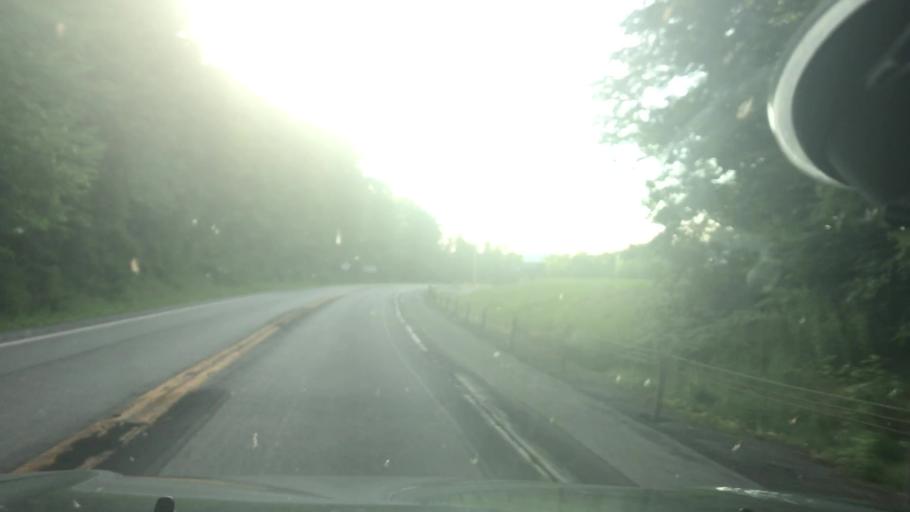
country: US
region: New York
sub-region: Otsego County
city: Unadilla
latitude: 42.3276
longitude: -75.2303
